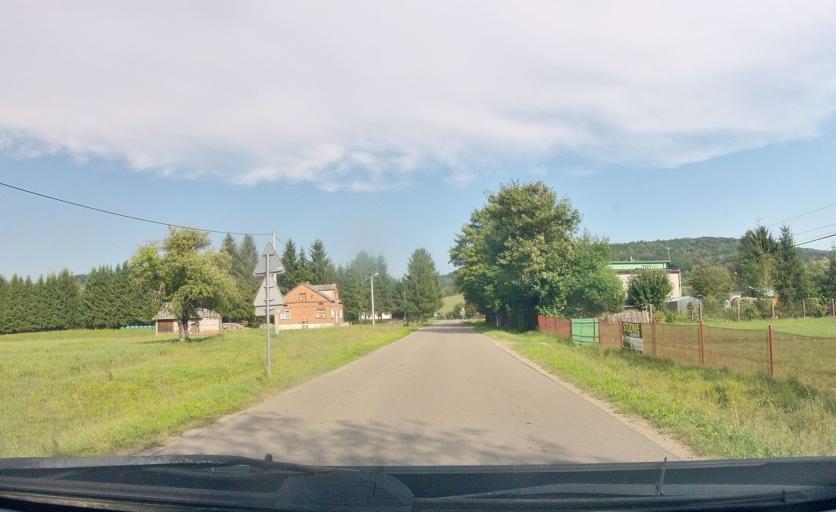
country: PL
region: Subcarpathian Voivodeship
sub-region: Powiat jasielski
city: Krempna
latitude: 49.4948
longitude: 21.5638
